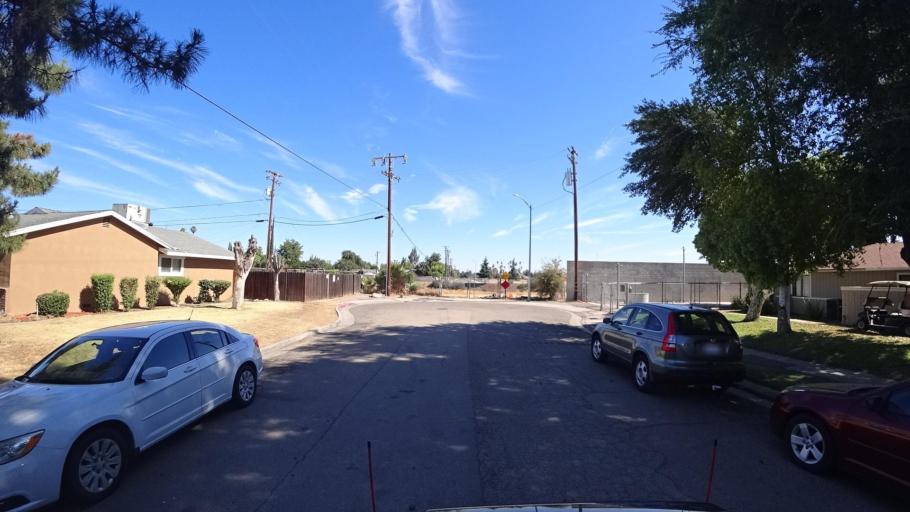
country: US
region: California
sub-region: Fresno County
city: Sunnyside
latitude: 36.7524
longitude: -119.7092
